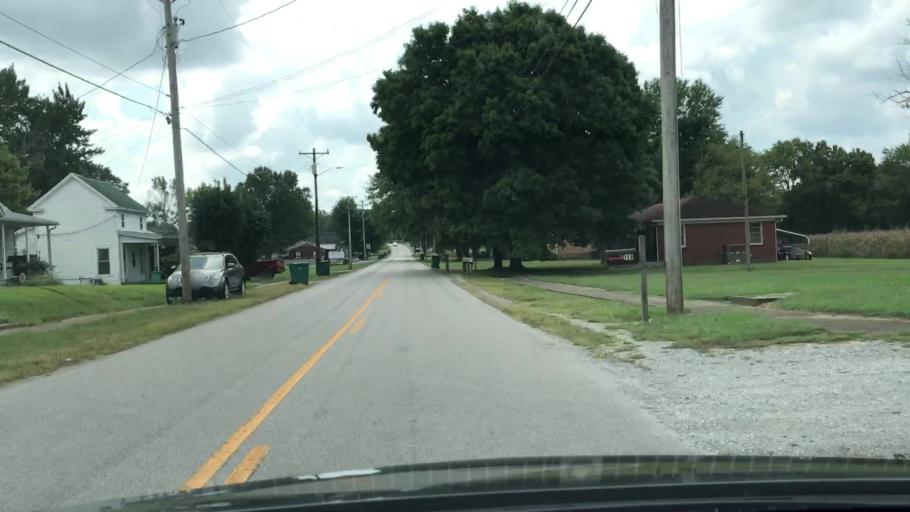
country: US
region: Kentucky
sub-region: Todd County
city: Elkton
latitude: 36.8071
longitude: -87.1480
